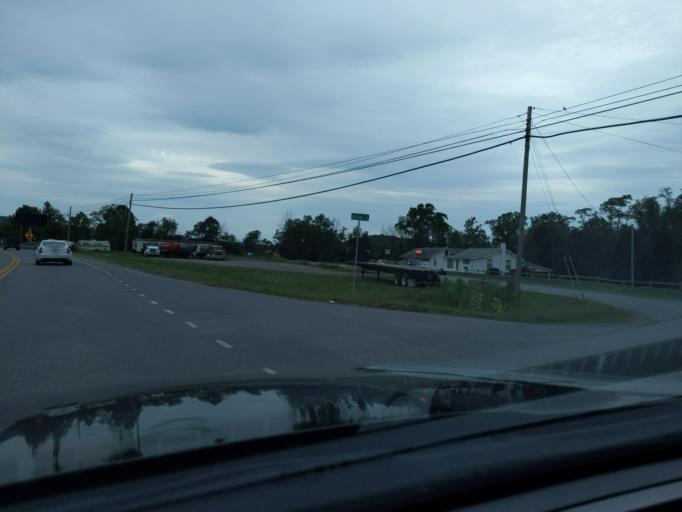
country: US
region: Pennsylvania
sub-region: Blair County
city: Duncansville
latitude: 40.4184
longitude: -78.4385
